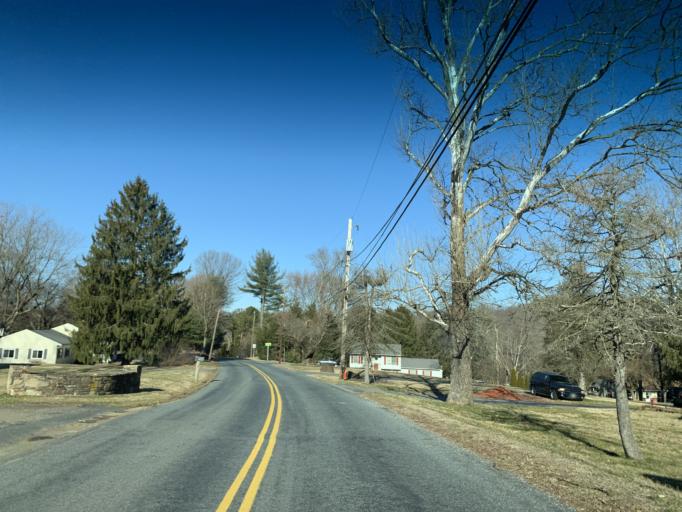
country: US
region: Maryland
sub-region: Harford County
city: South Bel Air
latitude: 39.6278
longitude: -76.2885
